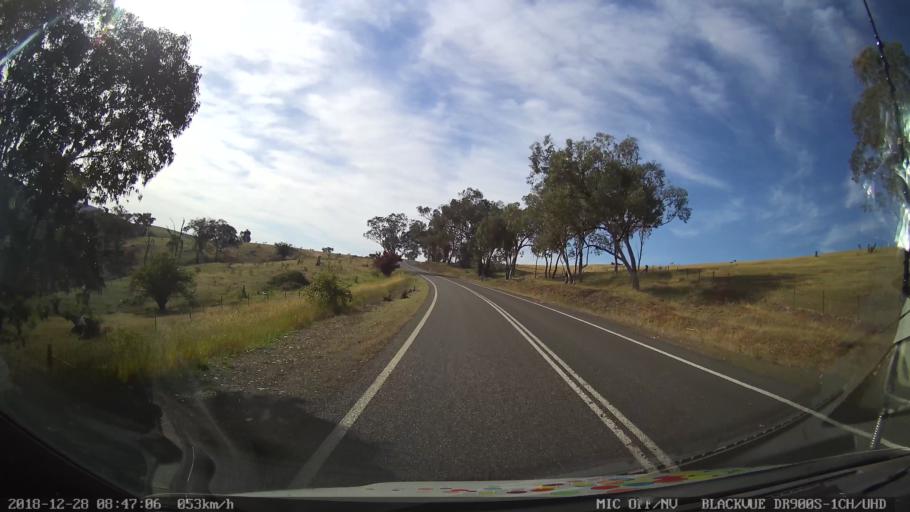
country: AU
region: New South Wales
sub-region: Upper Lachlan Shire
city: Crookwell
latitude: -34.0250
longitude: 149.3334
